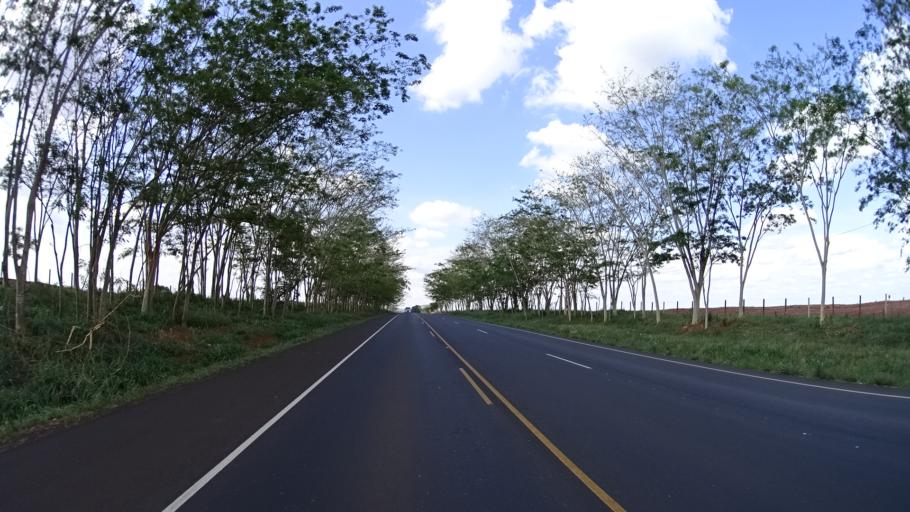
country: BR
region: Sao Paulo
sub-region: Urupes
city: Urupes
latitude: -21.0376
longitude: -49.2414
